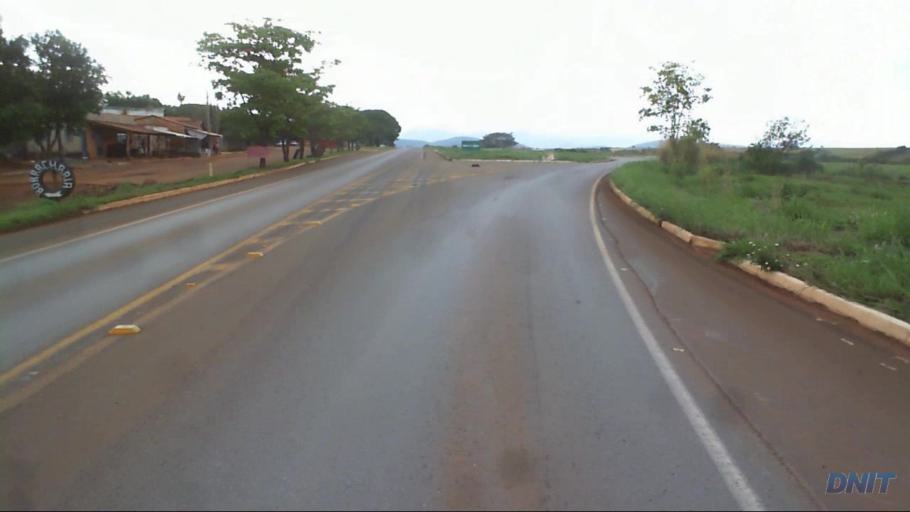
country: BR
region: Goias
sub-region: Barro Alto
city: Barro Alto
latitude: -14.8354
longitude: -49.0325
